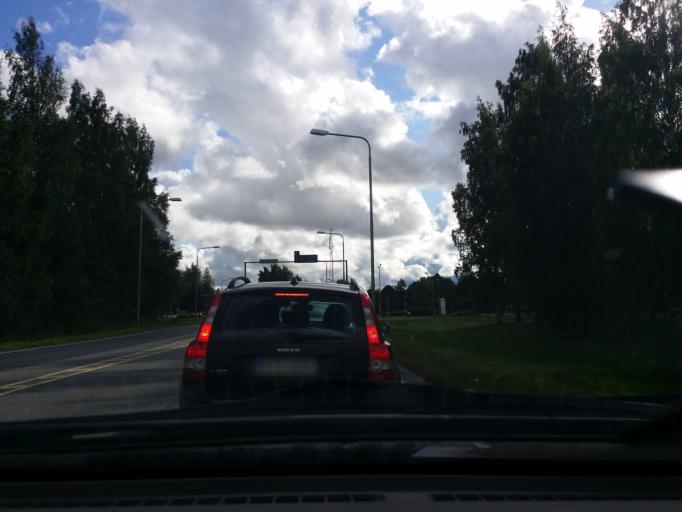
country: FI
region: Satakunta
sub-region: Pori
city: Pori
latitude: 61.4772
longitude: 21.8155
